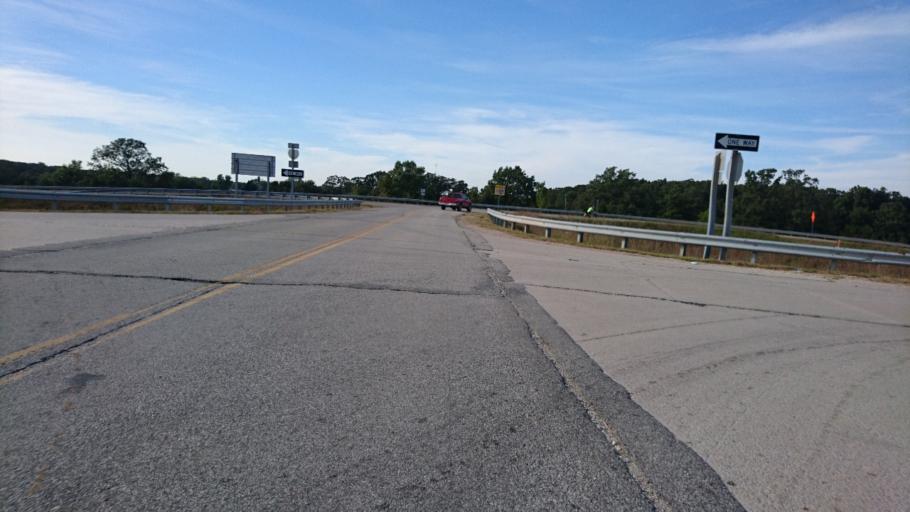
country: US
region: Missouri
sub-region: Crawford County
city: Cuba
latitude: 38.0940
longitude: -91.3689
